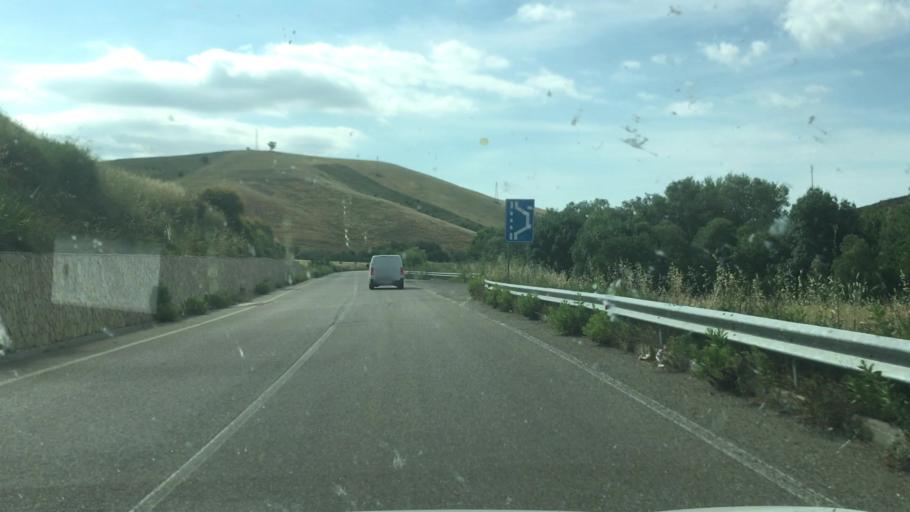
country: IT
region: Basilicate
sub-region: Provincia di Matera
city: Salandra
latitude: 40.5305
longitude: 16.2890
